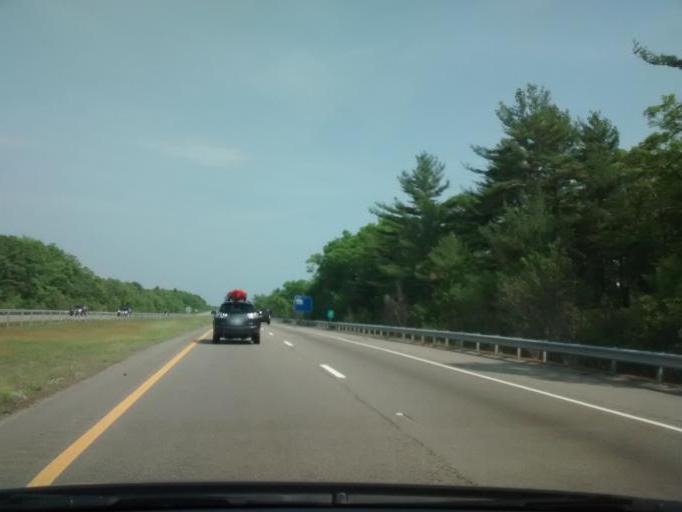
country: US
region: Massachusetts
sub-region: Plymouth County
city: Middleborough Center
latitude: 41.8865
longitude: -70.9311
